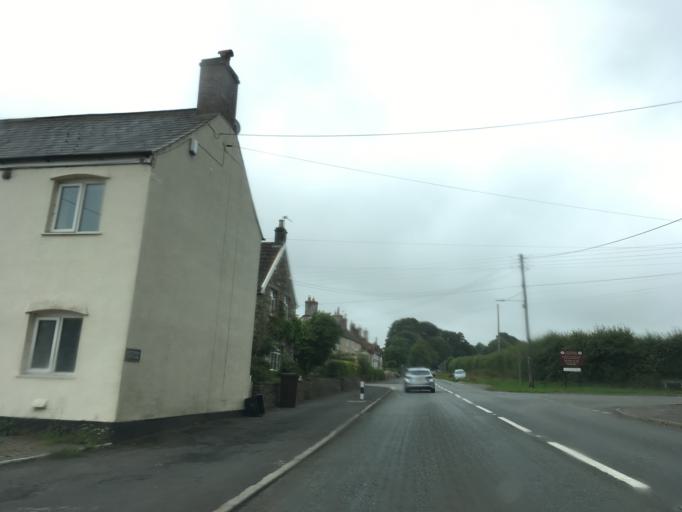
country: GB
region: England
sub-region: Bath and North East Somerset
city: East Harptree
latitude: 51.2696
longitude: -2.5863
